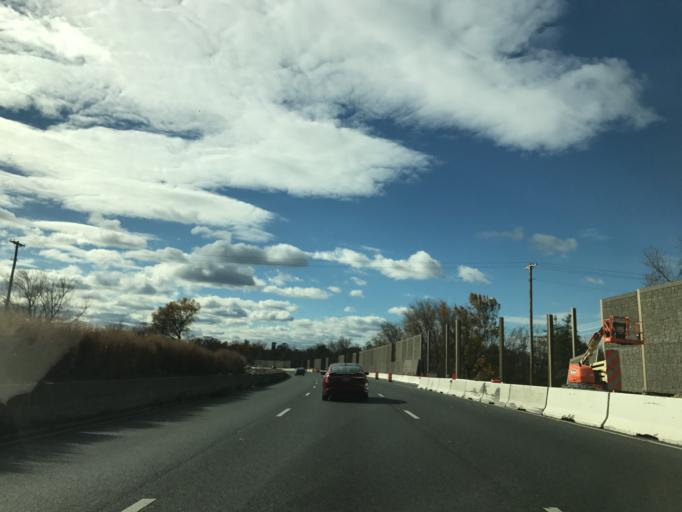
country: US
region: Maryland
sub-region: Baltimore County
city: Lansdowne
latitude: 39.2472
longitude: -76.6463
